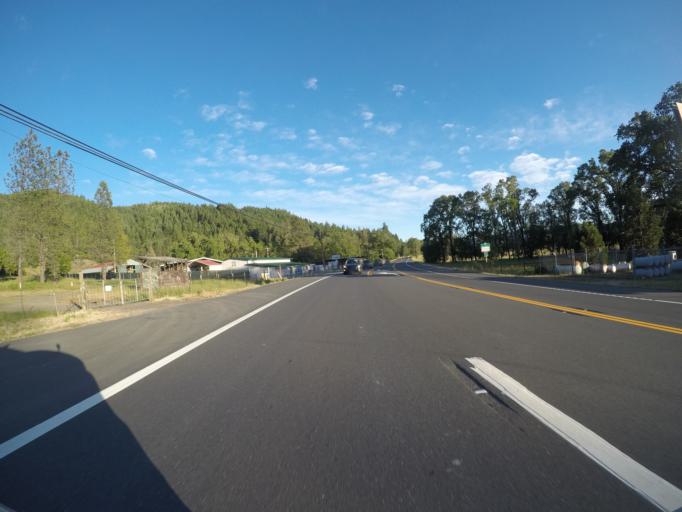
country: US
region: California
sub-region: Mendocino County
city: Laytonville
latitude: 39.6809
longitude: -123.4762
